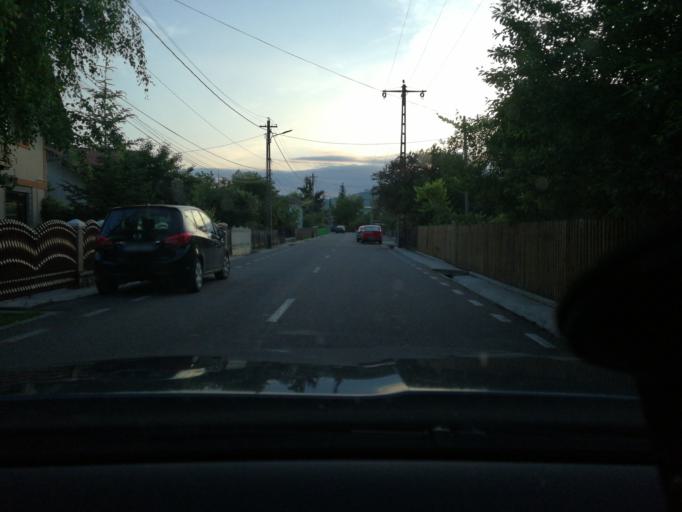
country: RO
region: Prahova
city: Cornu de Sus
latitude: 45.1616
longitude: 25.7018
